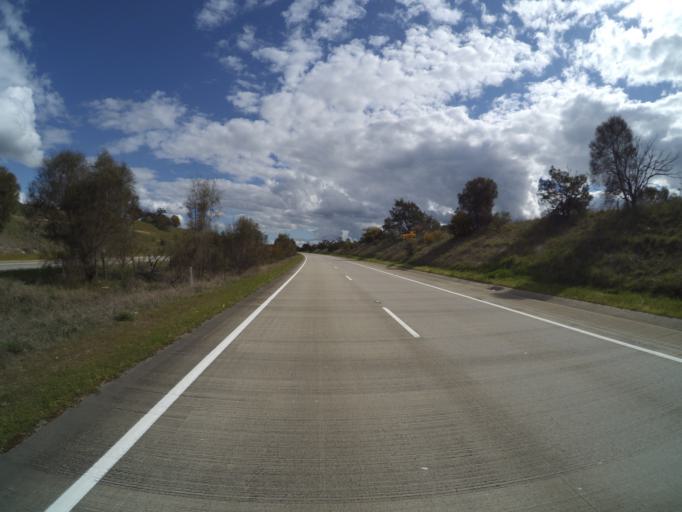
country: AU
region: New South Wales
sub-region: Yass Valley
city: Murrumbateman
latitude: -34.7876
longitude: 149.1778
